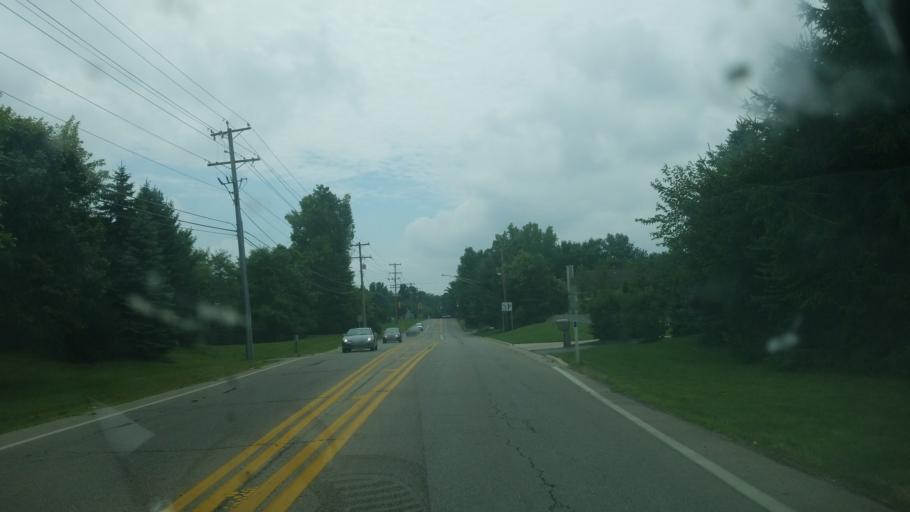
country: US
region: Ohio
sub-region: Franklin County
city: Reynoldsburg
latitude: 39.9753
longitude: -82.7931
